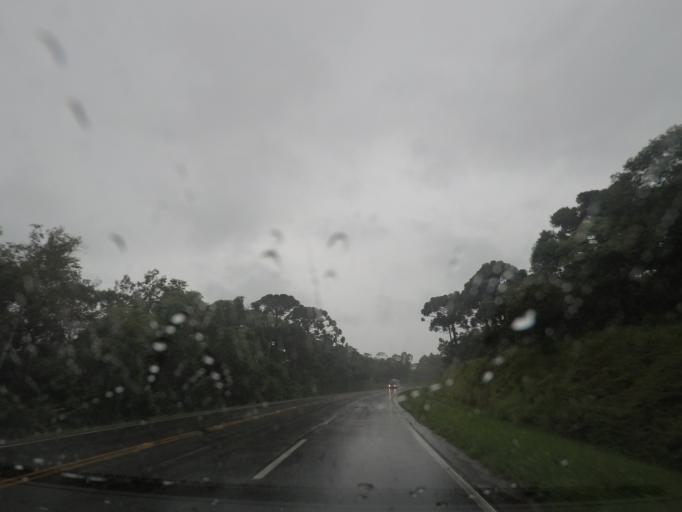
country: BR
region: Parana
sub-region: Almirante Tamandare
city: Almirante Tamandare
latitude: -25.3541
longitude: -49.3062
